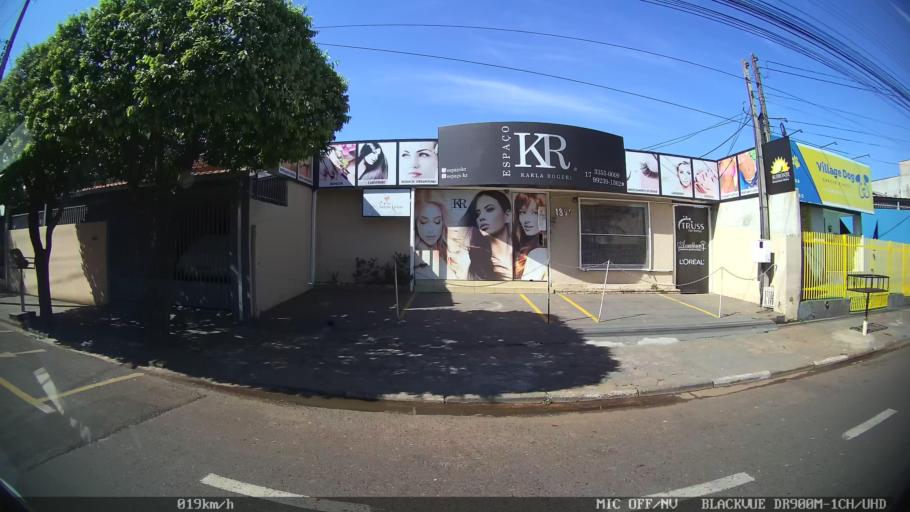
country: BR
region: Sao Paulo
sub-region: Sao Jose Do Rio Preto
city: Sao Jose do Rio Preto
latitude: -20.8048
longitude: -49.4008
